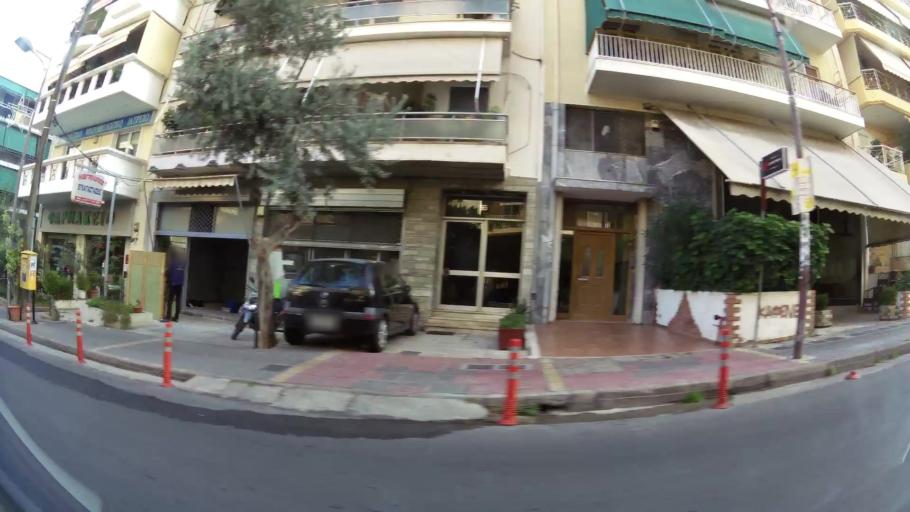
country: GR
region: Attica
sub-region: Nomarchia Athinas
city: Kaisariani
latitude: 37.9724
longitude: 23.7758
